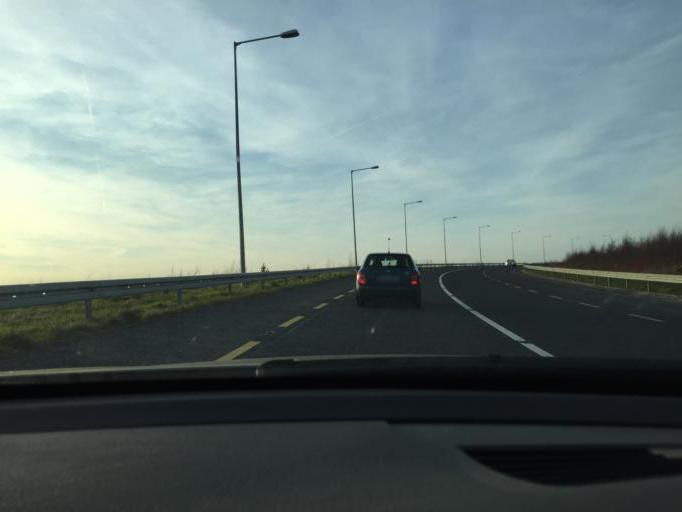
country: IE
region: Leinster
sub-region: An Mhi
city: Dunboyne
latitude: 53.4204
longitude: -6.4569
